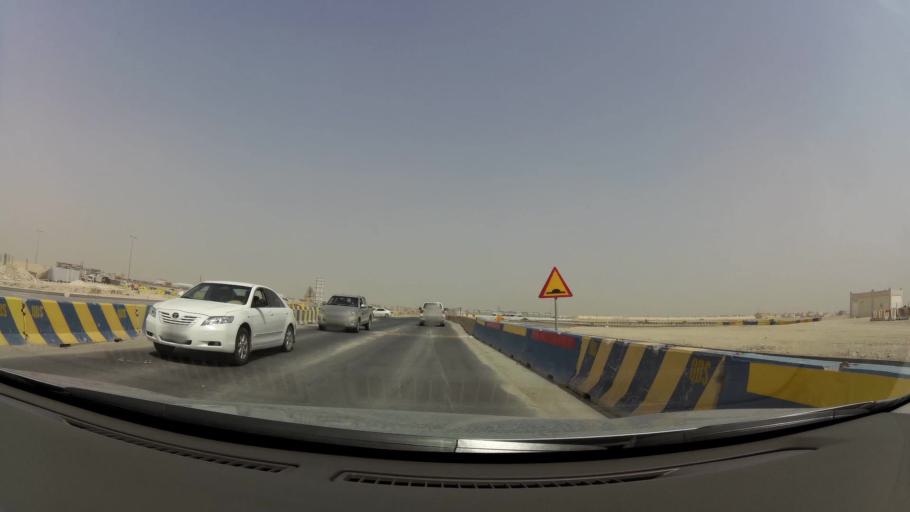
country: QA
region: Baladiyat ar Rayyan
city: Ar Rayyan
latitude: 25.2567
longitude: 51.3766
